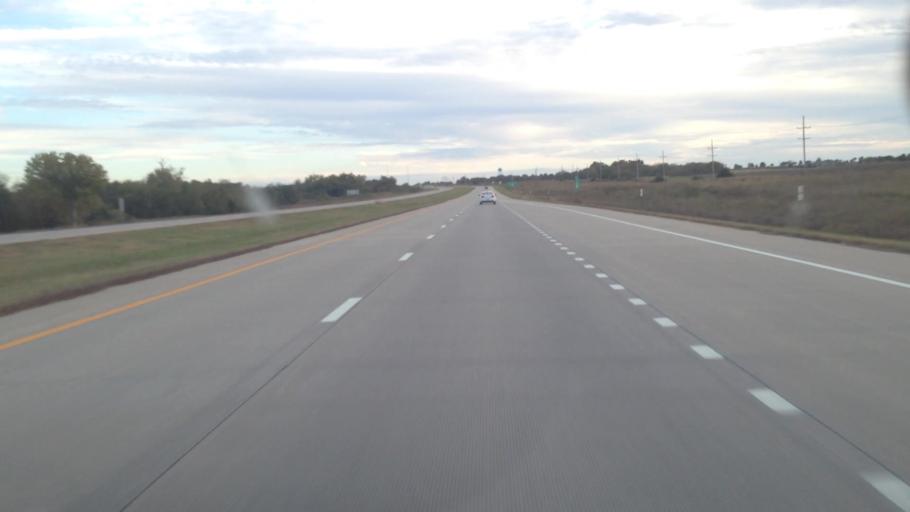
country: US
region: Kansas
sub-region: Franklin County
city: Ottawa
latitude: 38.7048
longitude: -95.2685
